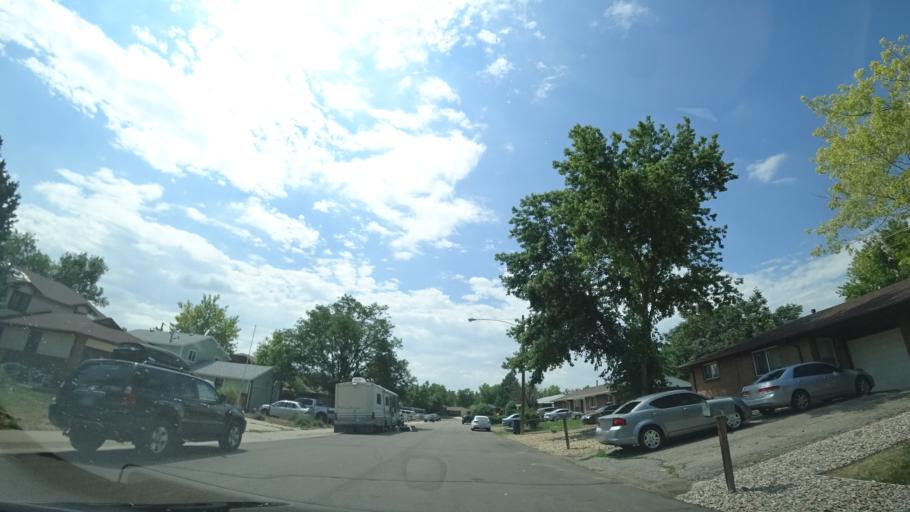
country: US
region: Colorado
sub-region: Jefferson County
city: Lakewood
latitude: 39.7177
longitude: -105.0731
